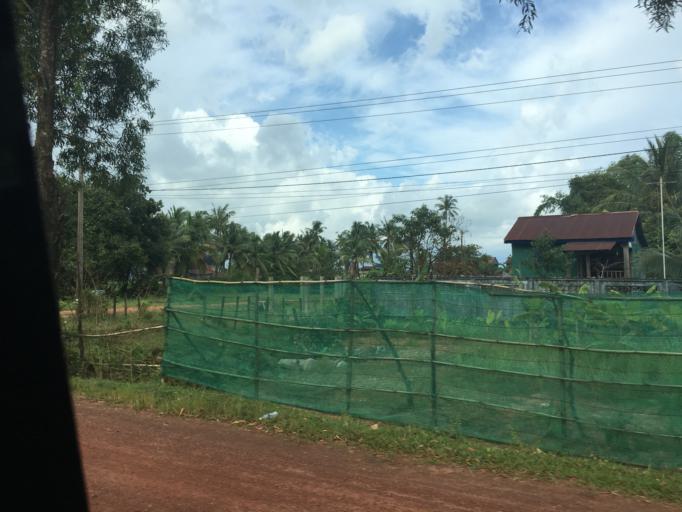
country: KH
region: Preah Sihanouk
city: Sihanoukville
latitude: 10.6492
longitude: 103.7883
